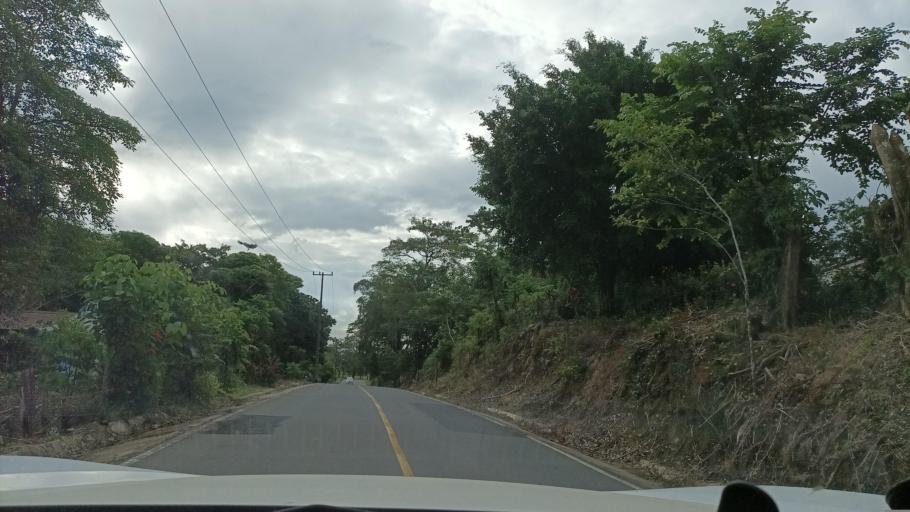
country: MX
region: Veracruz
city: Hidalgotitlan
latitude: 17.7298
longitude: -94.4836
